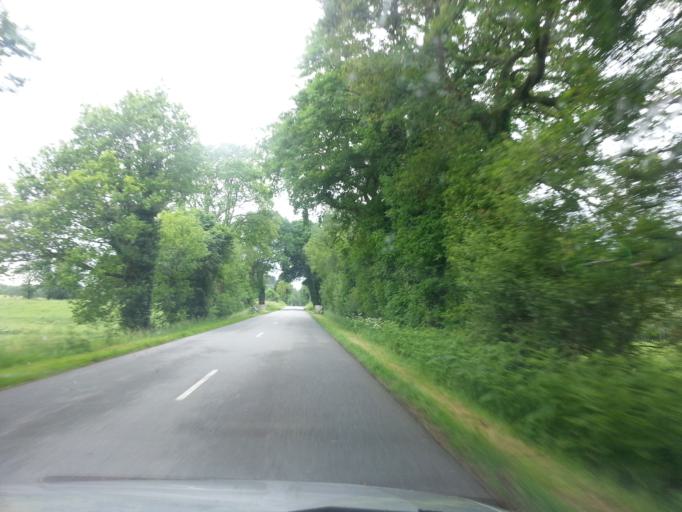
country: FR
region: Brittany
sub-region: Departement du Morbihan
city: Langonnet
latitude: 48.0792
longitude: -3.4638
